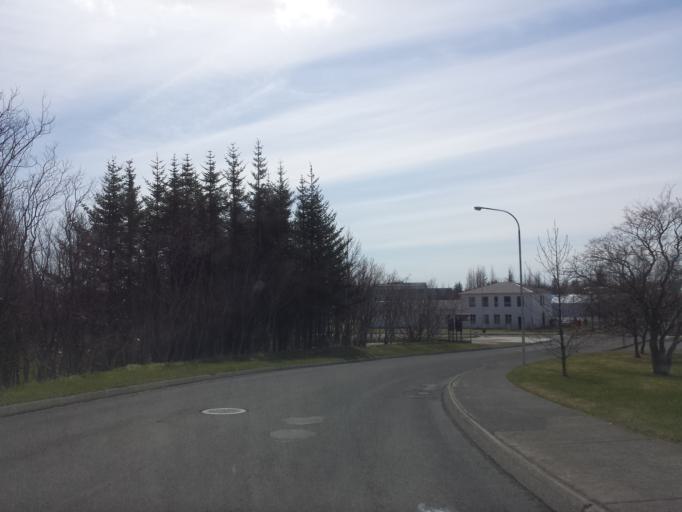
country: IS
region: South
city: Hveragerdi
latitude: 64.0020
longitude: -21.1840
